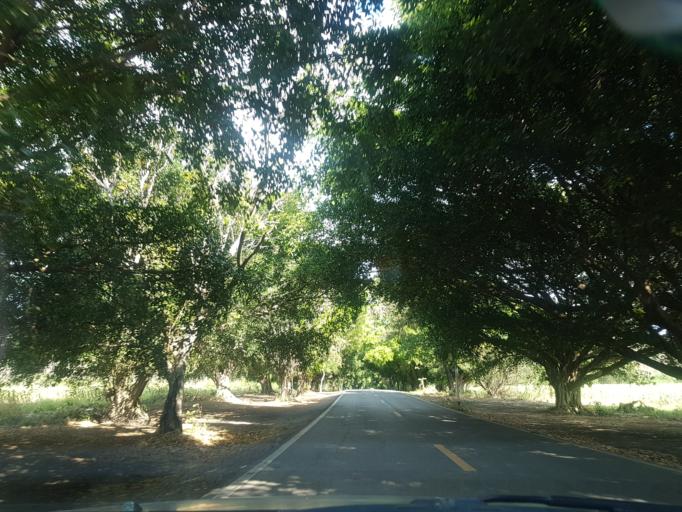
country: TH
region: Lop Buri
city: Lop Buri
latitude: 14.8151
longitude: 100.7517
